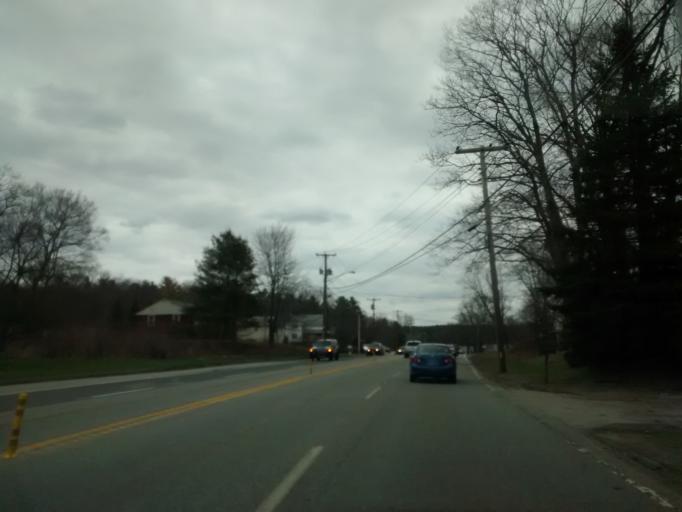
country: US
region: Massachusetts
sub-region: Worcester County
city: Oxford
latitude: 42.1680
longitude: -71.8911
